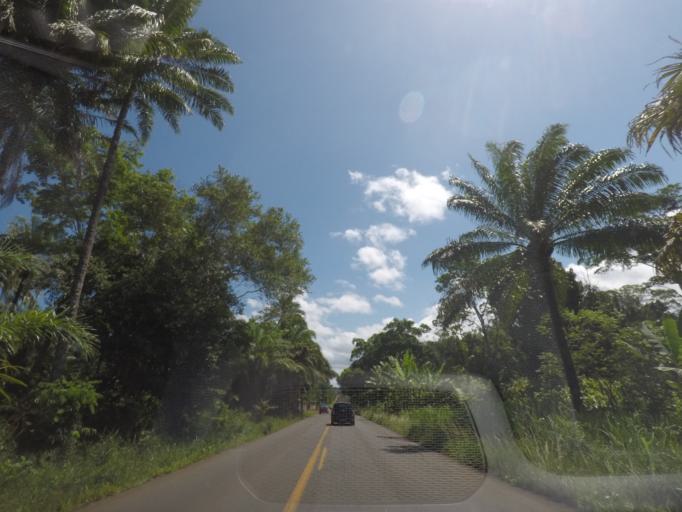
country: BR
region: Bahia
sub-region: Taperoa
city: Taperoa
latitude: -13.4745
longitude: -39.0893
